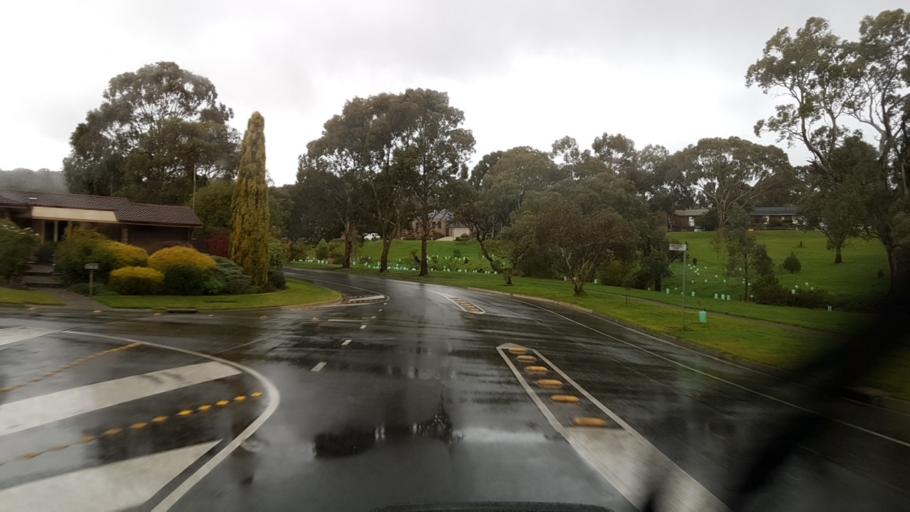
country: AU
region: South Australia
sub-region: Onkaparinga
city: Craigburn Farm
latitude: -35.0893
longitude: 138.5899
